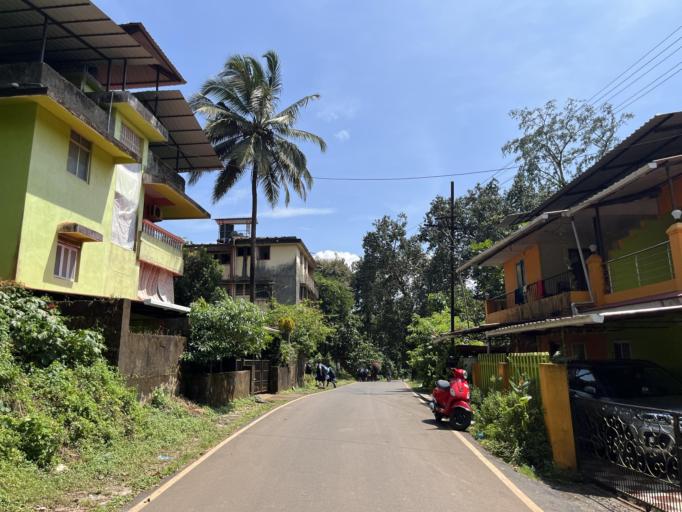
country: IN
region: Goa
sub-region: North Goa
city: Ponda
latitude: 15.3983
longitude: 74.0137
